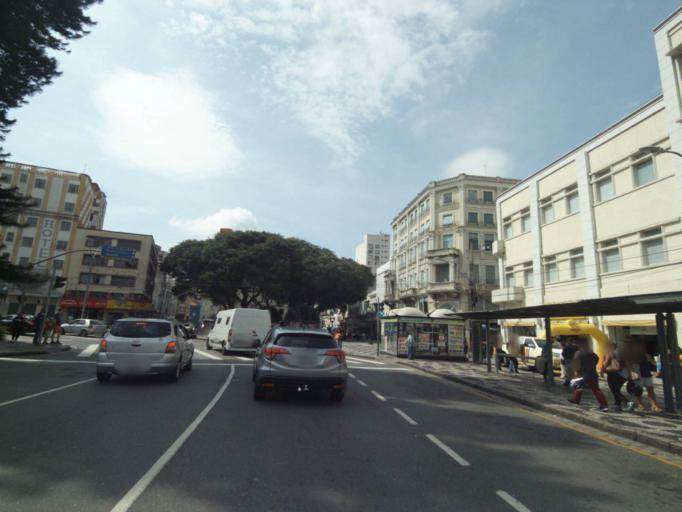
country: BR
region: Parana
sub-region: Curitiba
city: Curitiba
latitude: -25.4300
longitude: -49.2713
